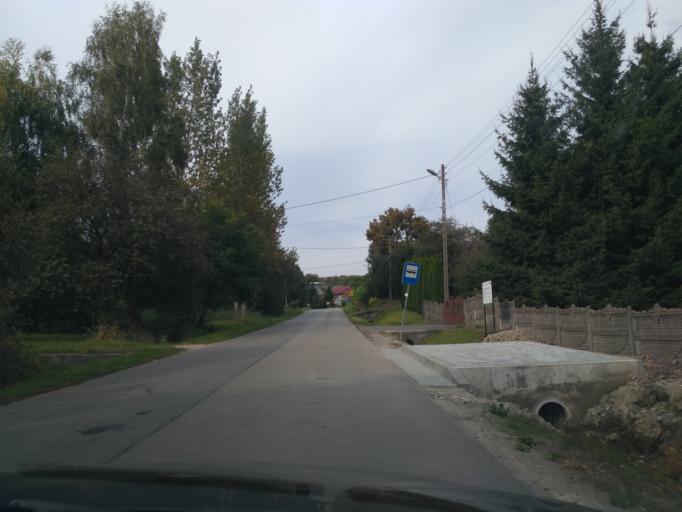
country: PL
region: Subcarpathian Voivodeship
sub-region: Powiat rzeszowski
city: Trzciana
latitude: 50.0439
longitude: 21.8336
